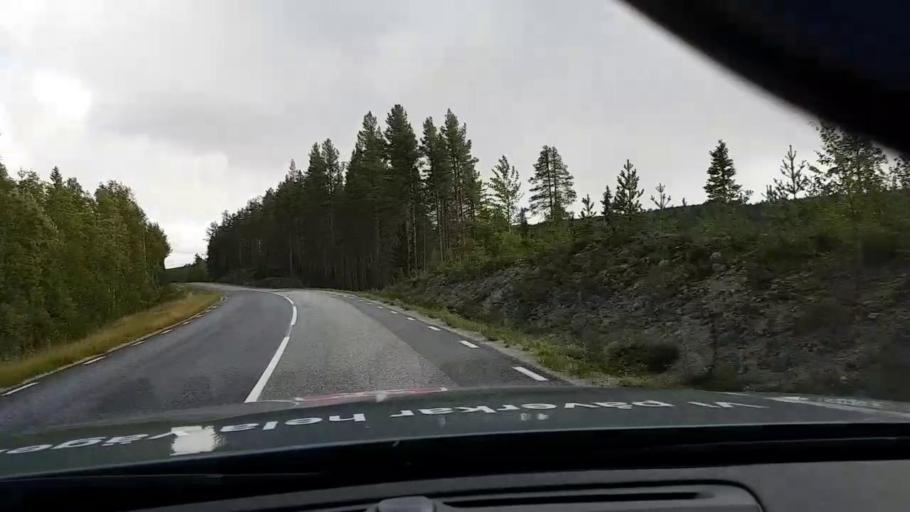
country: SE
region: Vaesterbotten
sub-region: Asele Kommun
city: Asele
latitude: 63.8430
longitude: 17.4239
